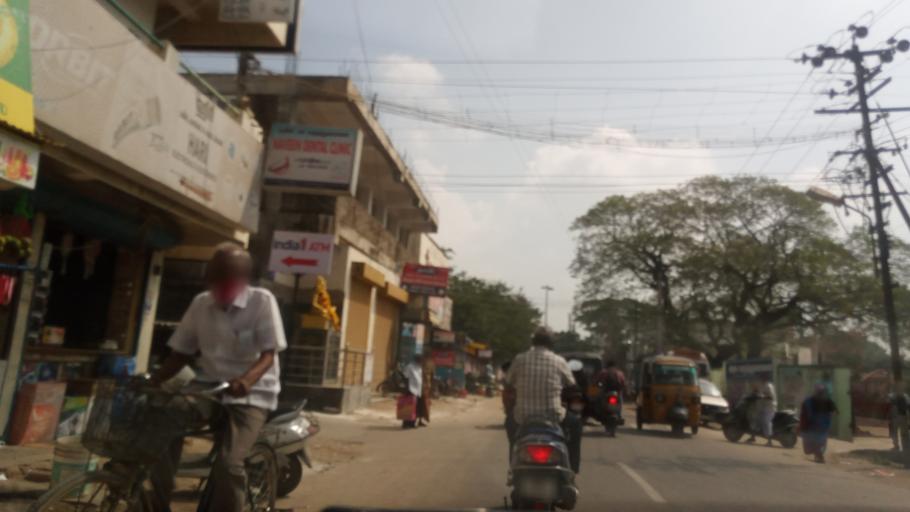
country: IN
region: Tamil Nadu
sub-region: Vellore
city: Arakkonam
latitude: 13.0854
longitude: 79.6647
